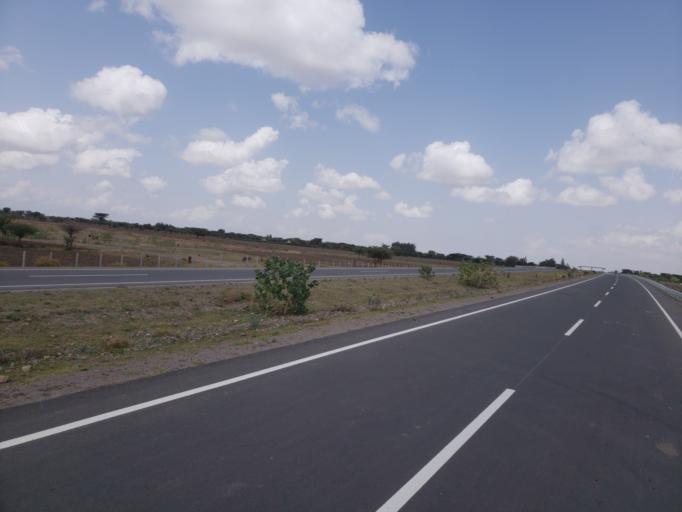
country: ET
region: Oromiya
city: Mojo
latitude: 8.2857
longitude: 38.9187
